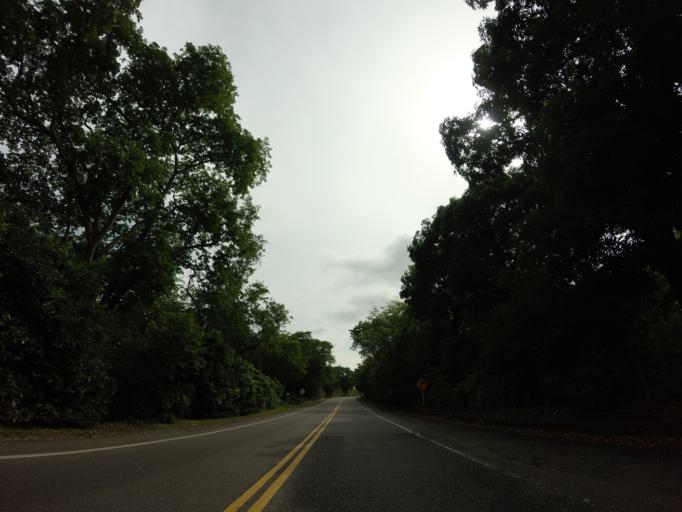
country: CO
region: Caldas
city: La Dorada
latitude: 5.4419
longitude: -74.6783
